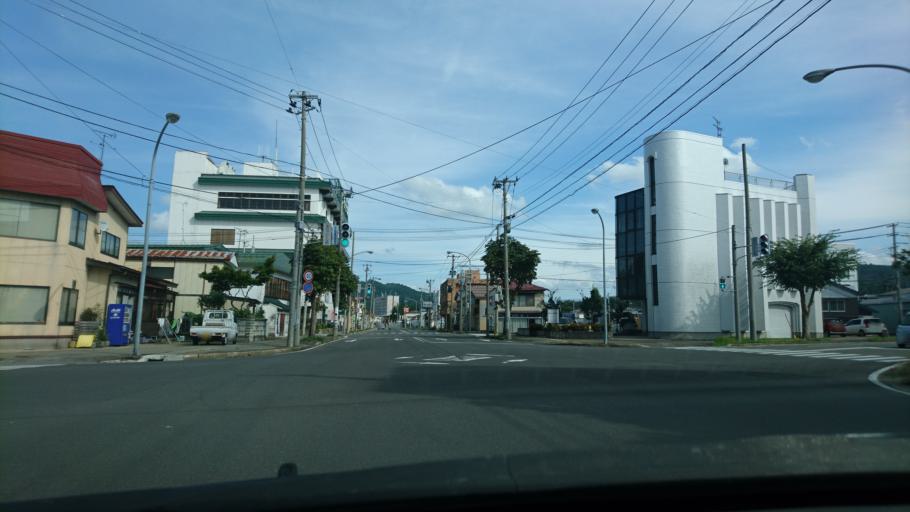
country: JP
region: Akita
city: Yokotemachi
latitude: 39.3096
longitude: 140.5679
